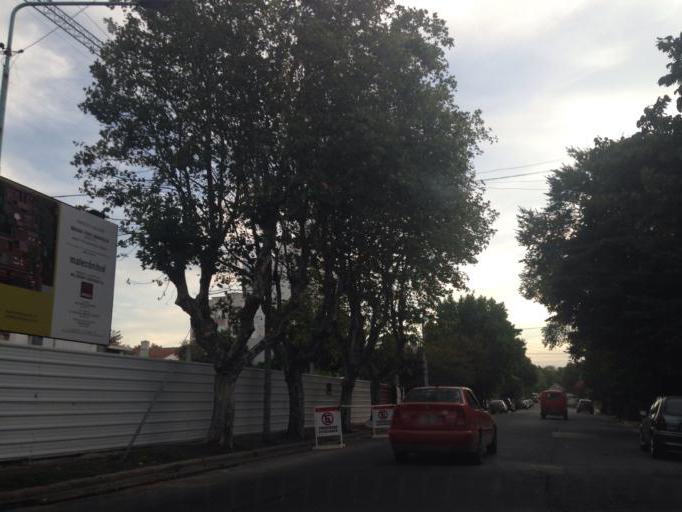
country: AR
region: Buenos Aires
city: Mar del Plata
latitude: -38.0171
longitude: -57.5456
